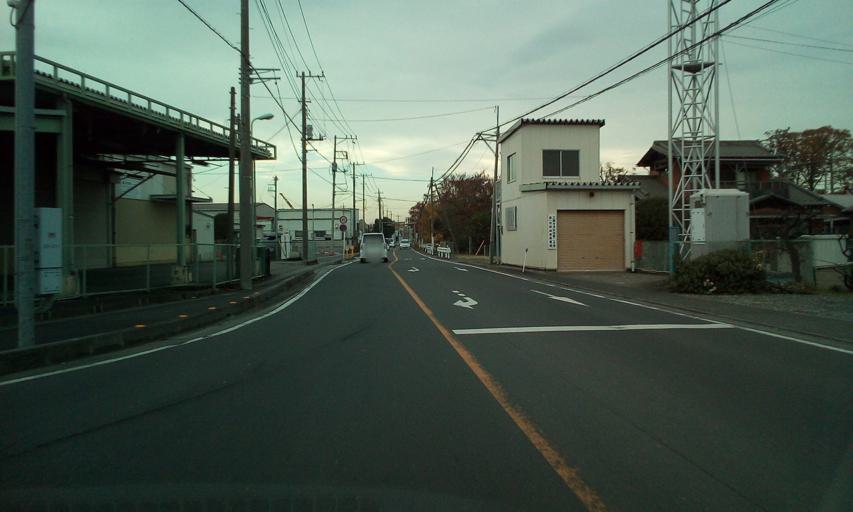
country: JP
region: Saitama
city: Yashio-shi
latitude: 35.8431
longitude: 139.8669
